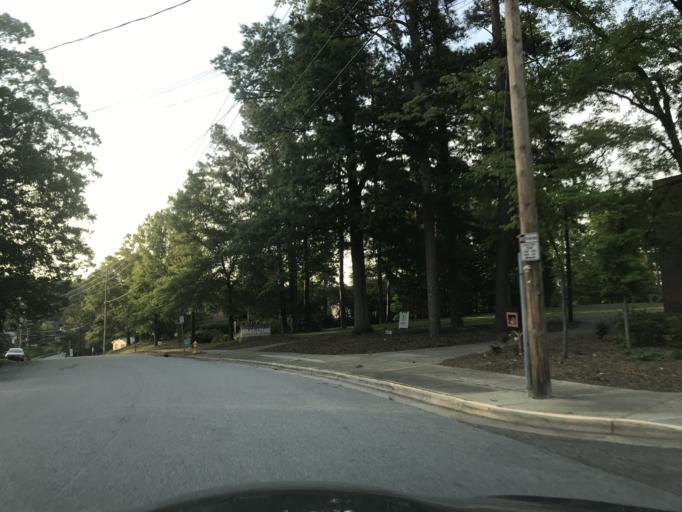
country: US
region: North Carolina
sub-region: Wake County
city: Raleigh
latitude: 35.7949
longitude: -78.6041
